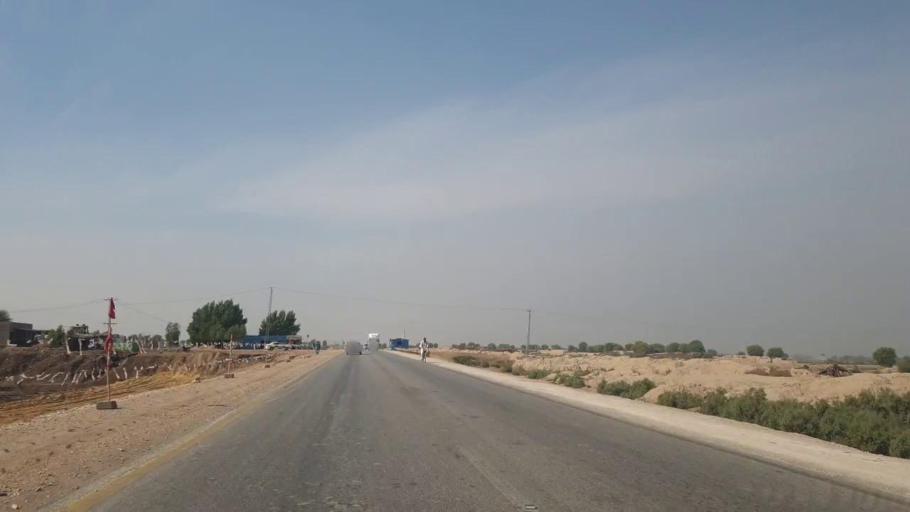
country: PK
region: Sindh
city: Sann
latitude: 25.9984
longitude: 68.1652
